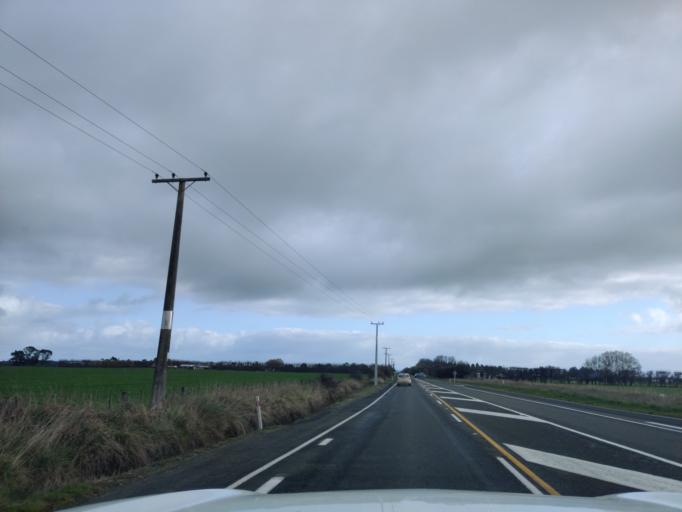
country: NZ
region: Manawatu-Wanganui
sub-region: Palmerston North City
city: Palmerston North
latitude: -40.3323
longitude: 175.5899
